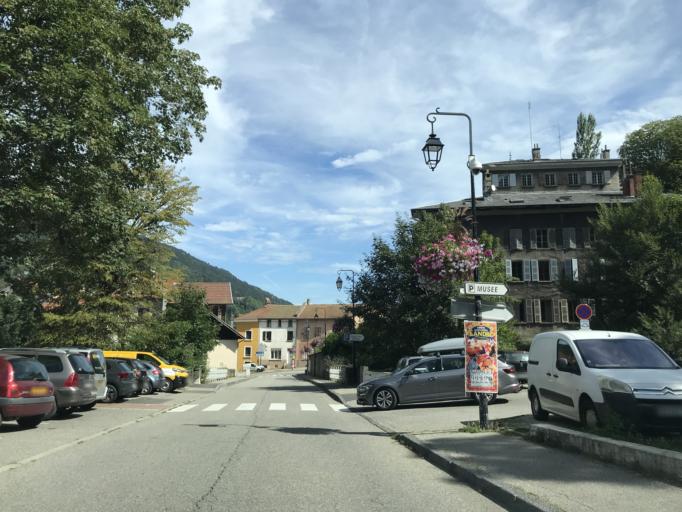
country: FR
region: Rhone-Alpes
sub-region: Departement de l'Isere
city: Allevard
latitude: 45.3926
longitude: 6.0756
